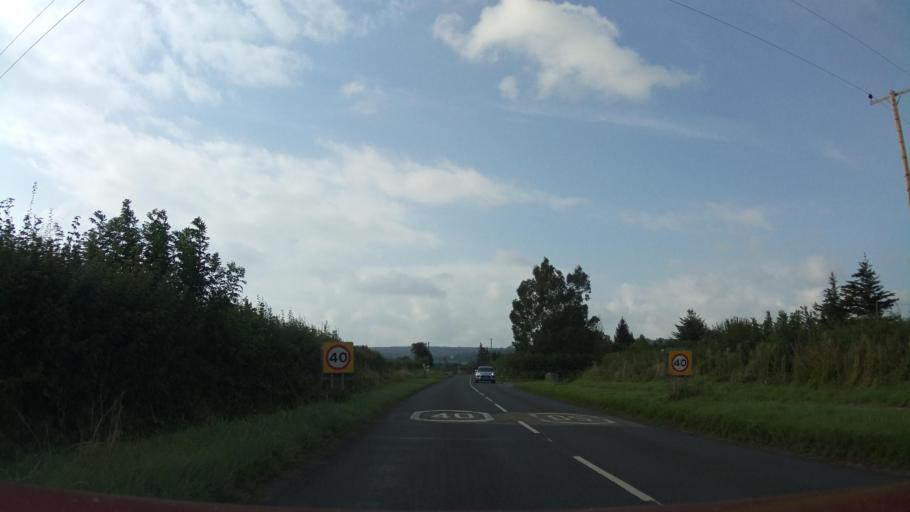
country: GB
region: England
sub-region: Bath and North East Somerset
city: Compton Martin
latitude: 51.3245
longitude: -2.6406
